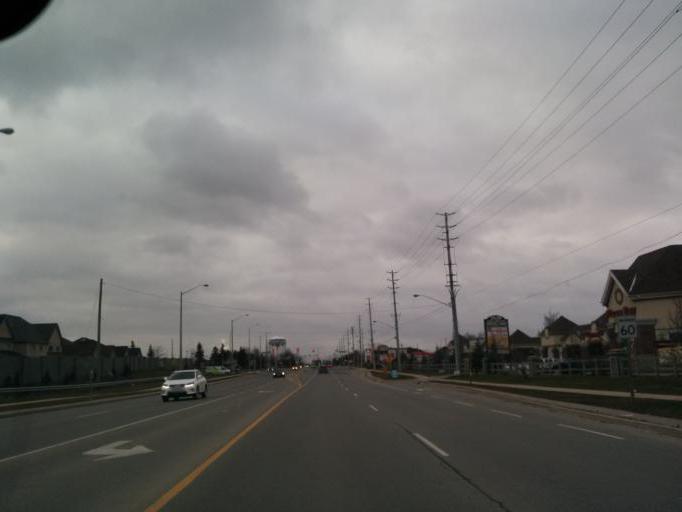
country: CA
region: Ontario
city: Brampton
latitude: 43.7362
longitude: -79.8223
